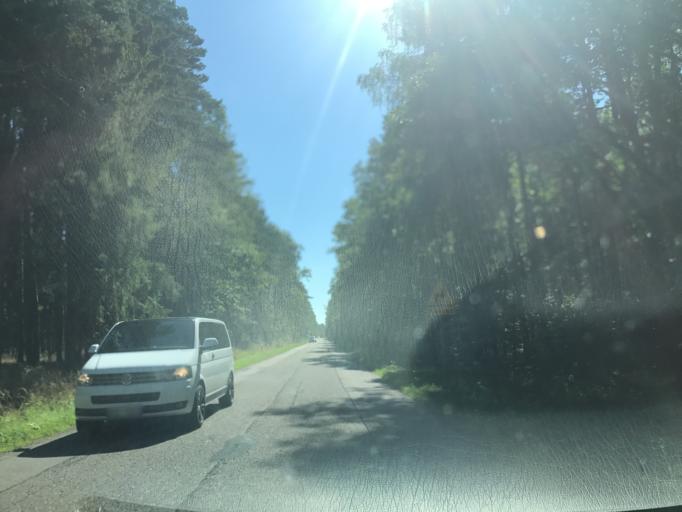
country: PL
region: Pomeranian Voivodeship
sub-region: Powiat bytowski
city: Czarna Dabrowka
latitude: 54.3435
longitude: 17.5996
